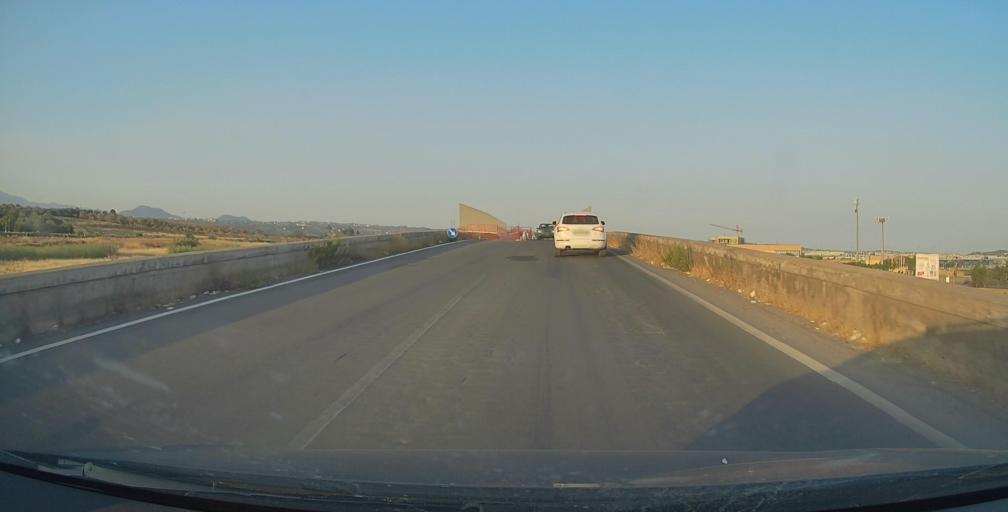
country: IT
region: Sicily
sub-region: Catania
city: Palazzolo
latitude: 37.5489
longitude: 14.9407
